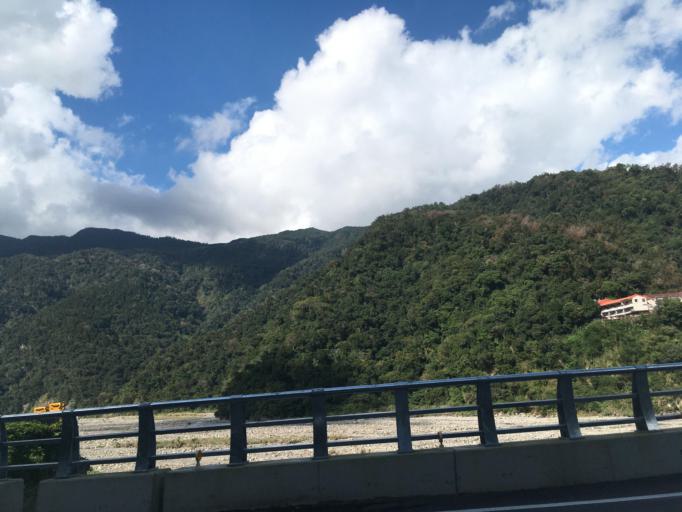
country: TW
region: Taiwan
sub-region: Yilan
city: Yilan
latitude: 24.5771
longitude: 121.4917
